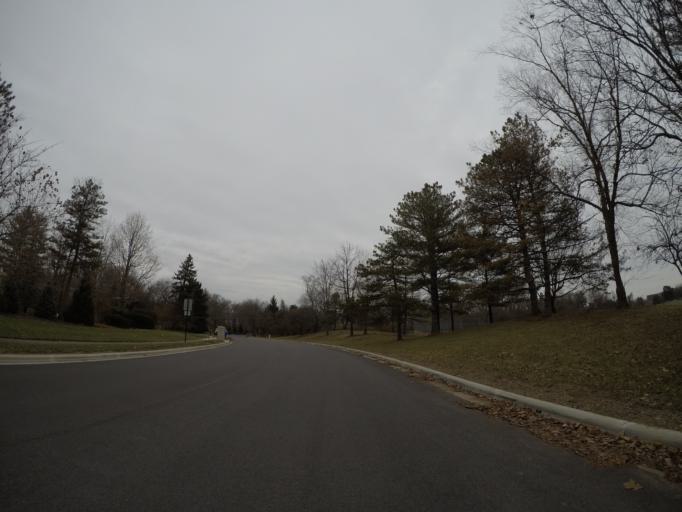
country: US
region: Ohio
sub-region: Franklin County
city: Dublin
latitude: 40.0567
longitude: -83.0850
